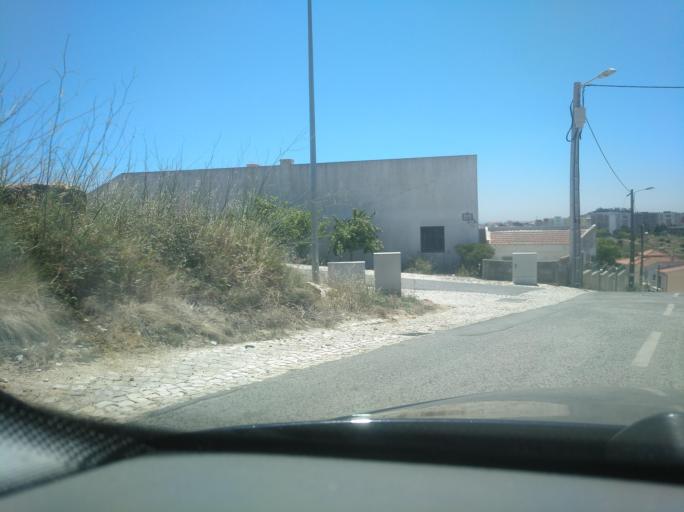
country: PT
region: Lisbon
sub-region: Odivelas
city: Canecas
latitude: 38.8054
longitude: -9.2363
